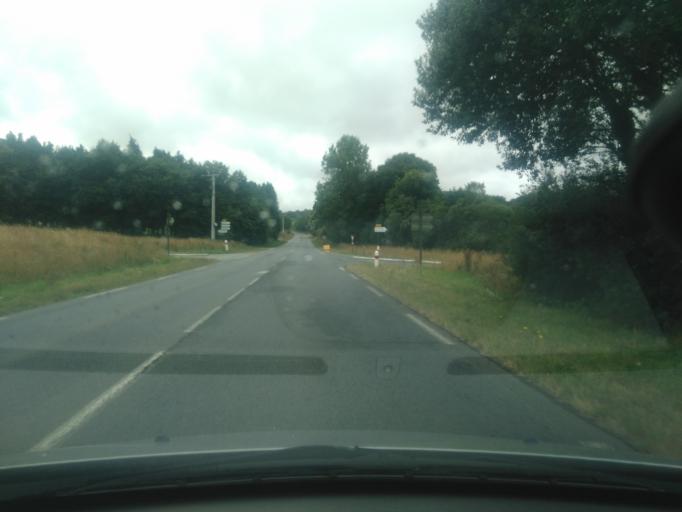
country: FR
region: Brittany
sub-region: Departement des Cotes-d'Armor
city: Quintin
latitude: 48.3683
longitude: -2.9477
